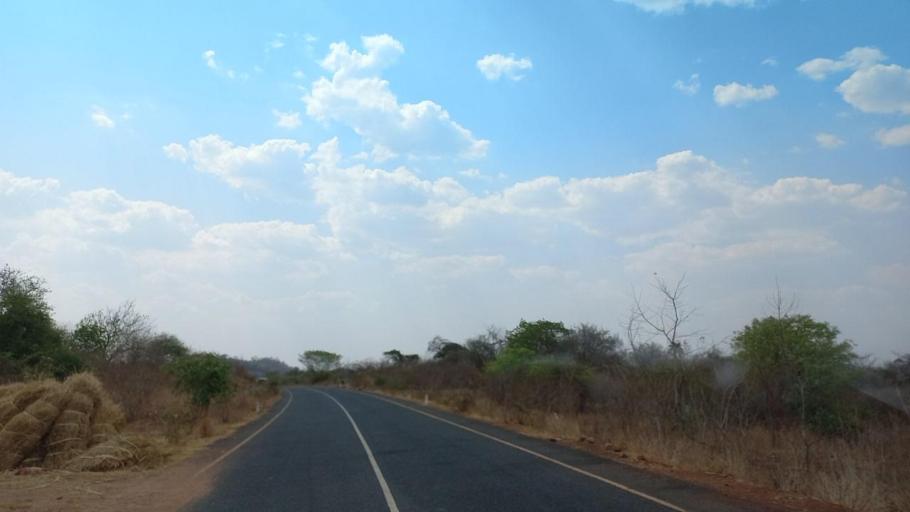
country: ZM
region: Lusaka
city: Luangwa
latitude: -15.3204
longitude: 30.3378
